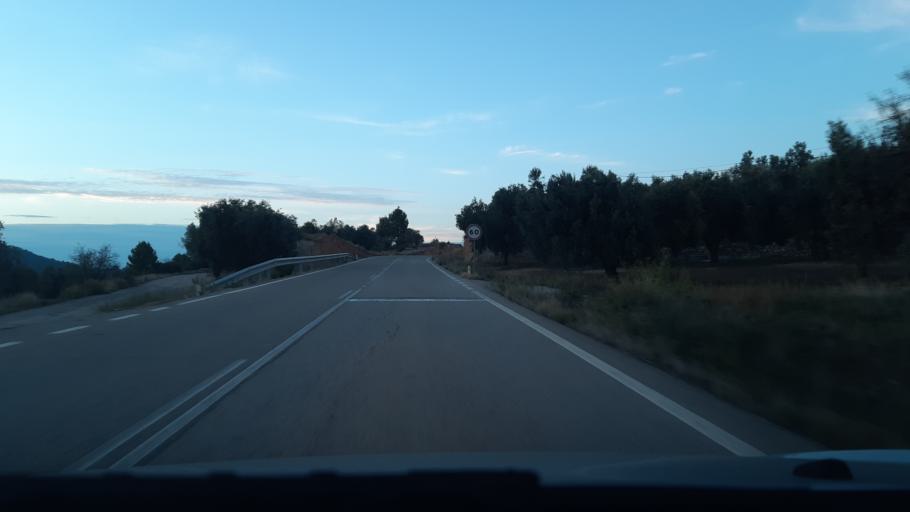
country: ES
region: Aragon
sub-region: Provincia de Teruel
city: Valderrobres
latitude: 40.8582
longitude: 0.1700
